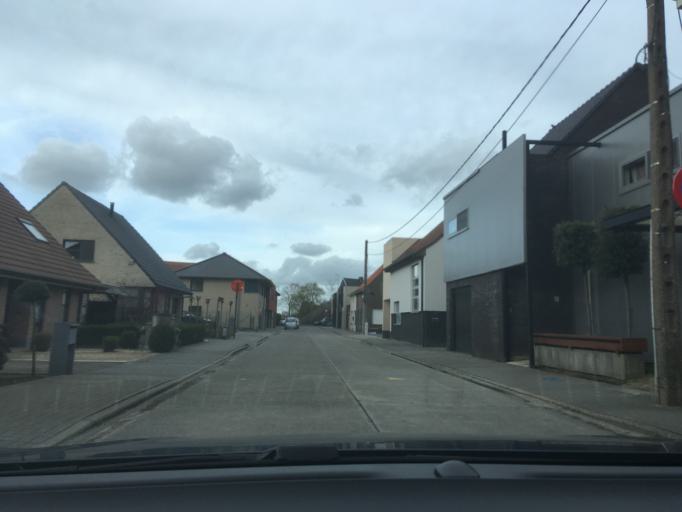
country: BE
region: Flanders
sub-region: Provincie West-Vlaanderen
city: Wielsbeke
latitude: 50.9076
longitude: 3.3662
